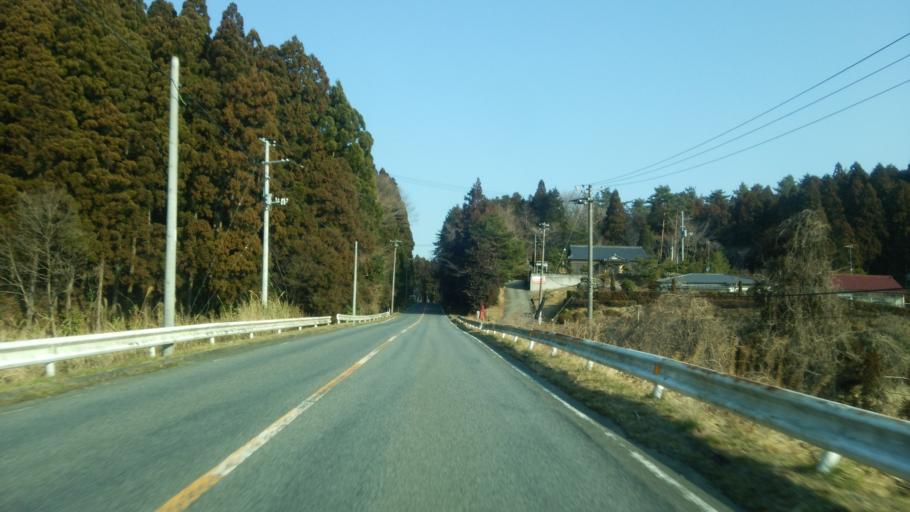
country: JP
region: Fukushima
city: Iwaki
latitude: 37.0582
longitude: 140.8027
